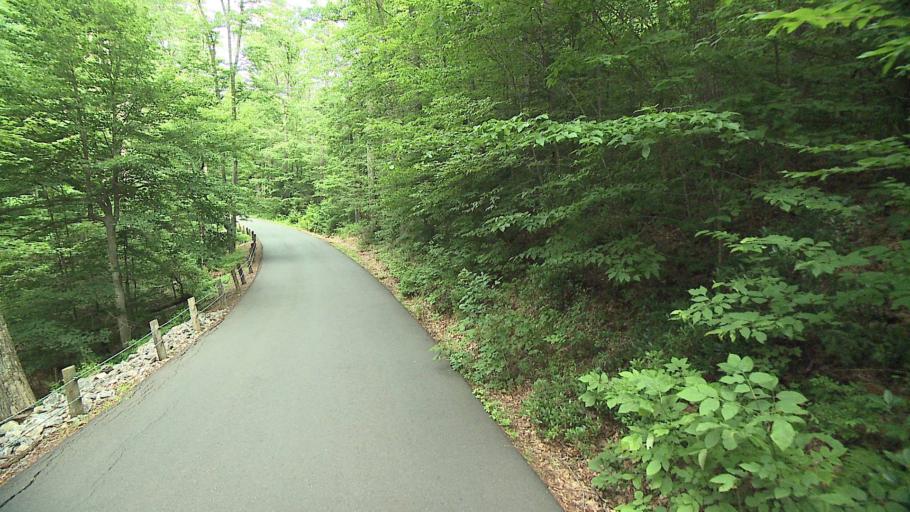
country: US
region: Connecticut
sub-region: Litchfield County
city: Winsted
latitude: 41.9435
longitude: -73.0080
